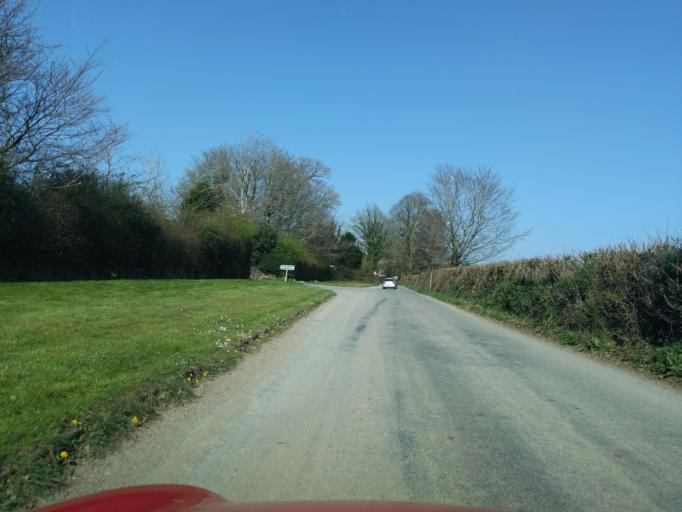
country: GB
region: England
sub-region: Devon
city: Horrabridge
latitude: 50.4793
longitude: -4.1295
